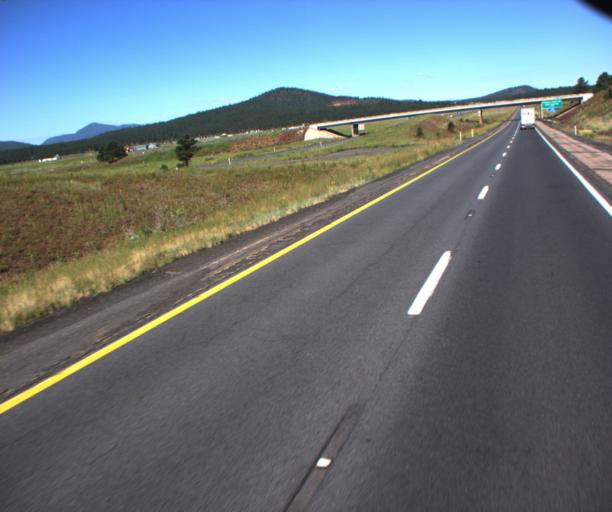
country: US
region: Arizona
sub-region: Coconino County
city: Parks
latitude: 35.2597
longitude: -112.0279
